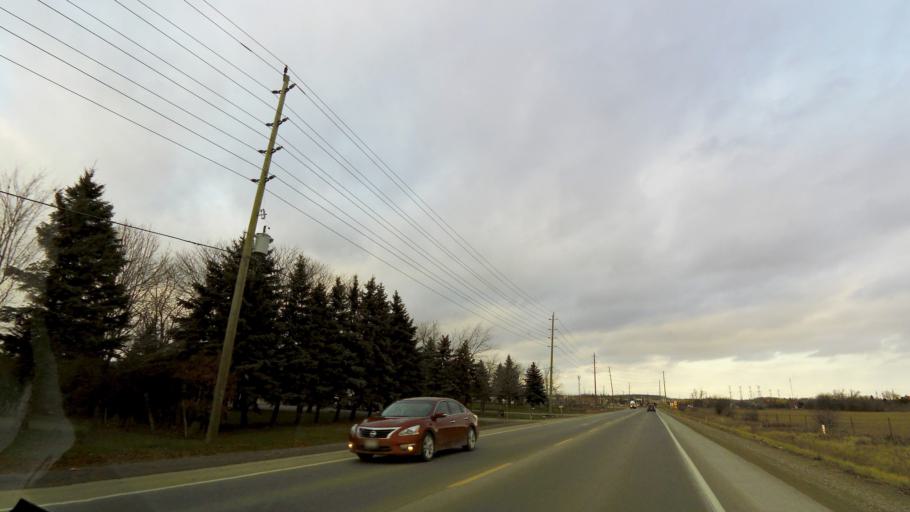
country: CA
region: Ontario
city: Brampton
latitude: 43.8438
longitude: -79.7001
